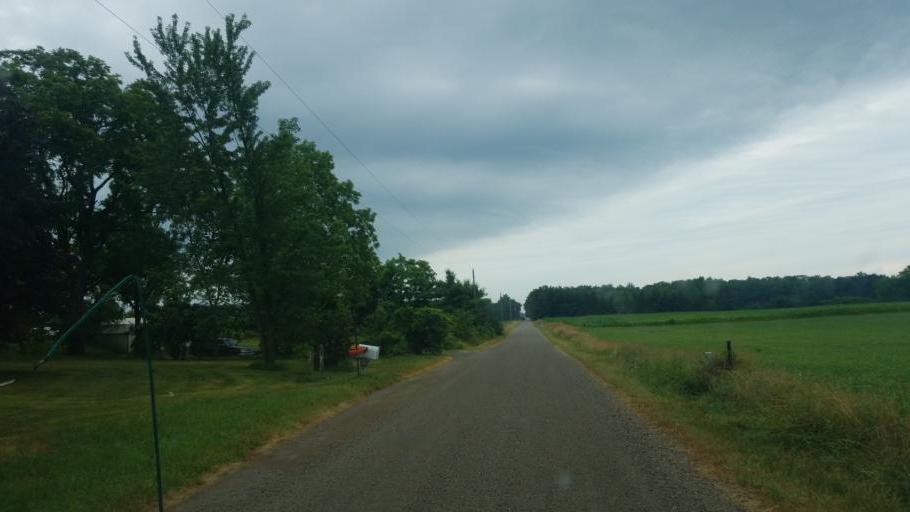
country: US
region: Indiana
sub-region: Steuben County
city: Hamilton
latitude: 41.4854
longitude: -84.9107
